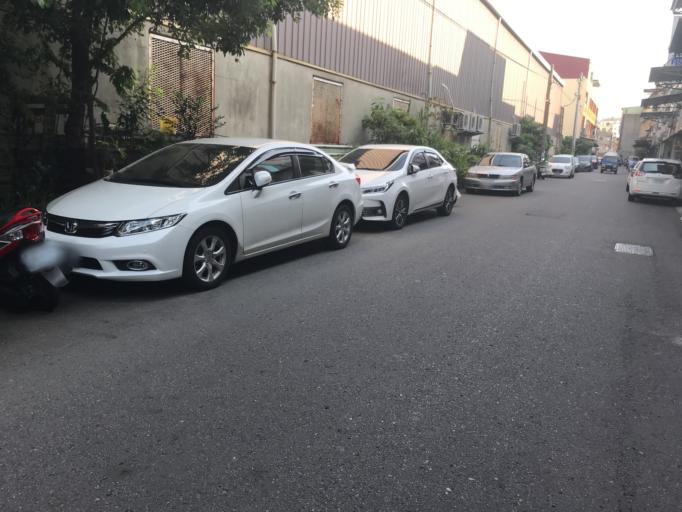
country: TW
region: Taiwan
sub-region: Changhua
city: Chang-hua
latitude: 24.0872
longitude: 120.5556
